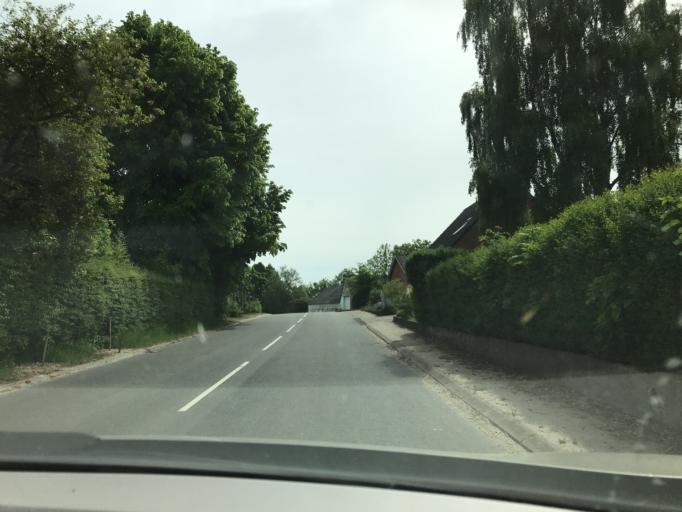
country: DK
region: Central Jutland
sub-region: Norddjurs Kommune
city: Allingabro
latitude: 56.5530
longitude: 10.2988
